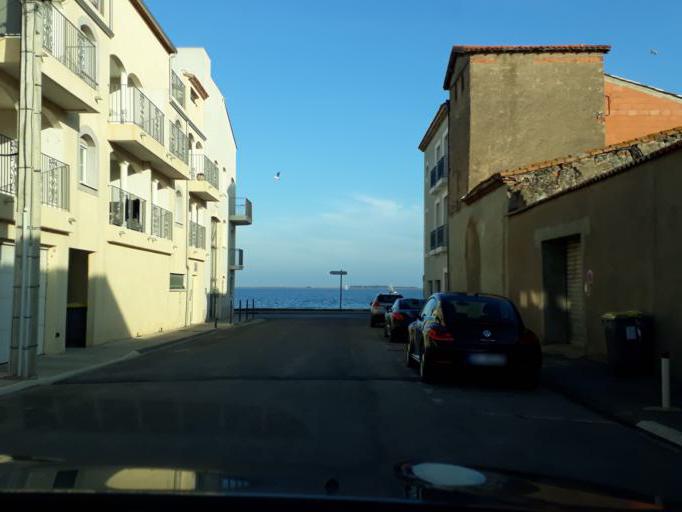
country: FR
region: Languedoc-Roussillon
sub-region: Departement de l'Herault
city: Marseillan
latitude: 43.3539
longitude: 3.5340
